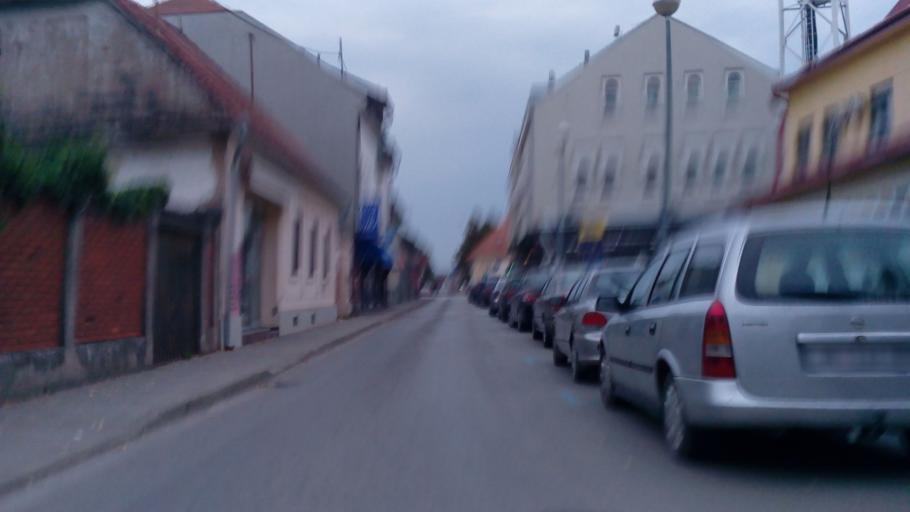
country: HR
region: Vukovarsko-Srijemska
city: Vinkovci
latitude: 45.2901
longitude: 18.8045
